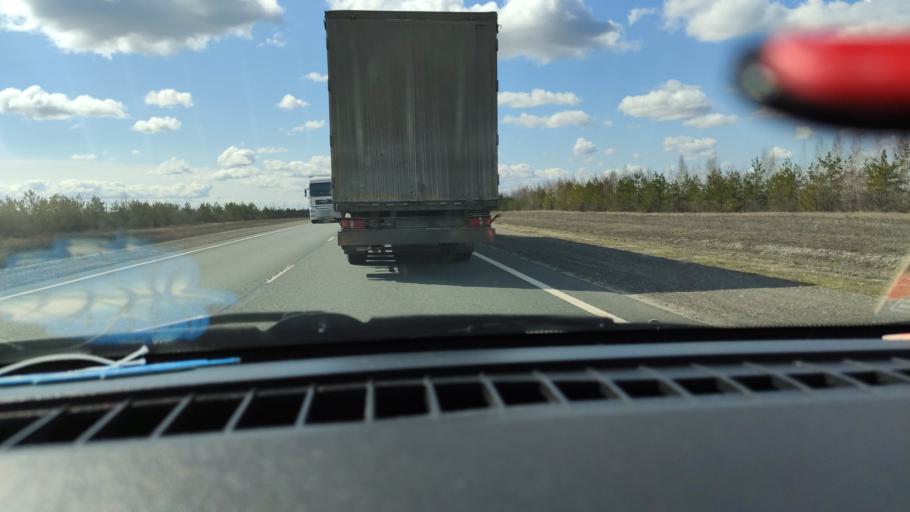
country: RU
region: Samara
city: Syzran'
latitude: 52.8764
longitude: 48.2901
